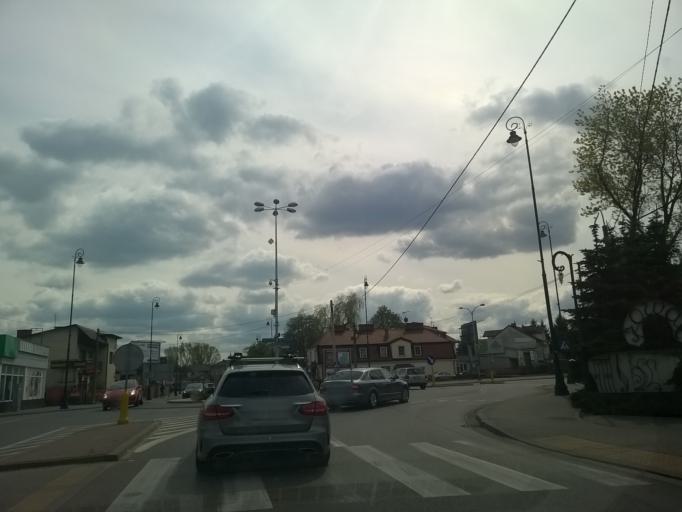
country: PL
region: Masovian Voivodeship
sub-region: Powiat piaseczynski
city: Konstancin-Jeziorna
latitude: 52.0941
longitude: 21.1175
